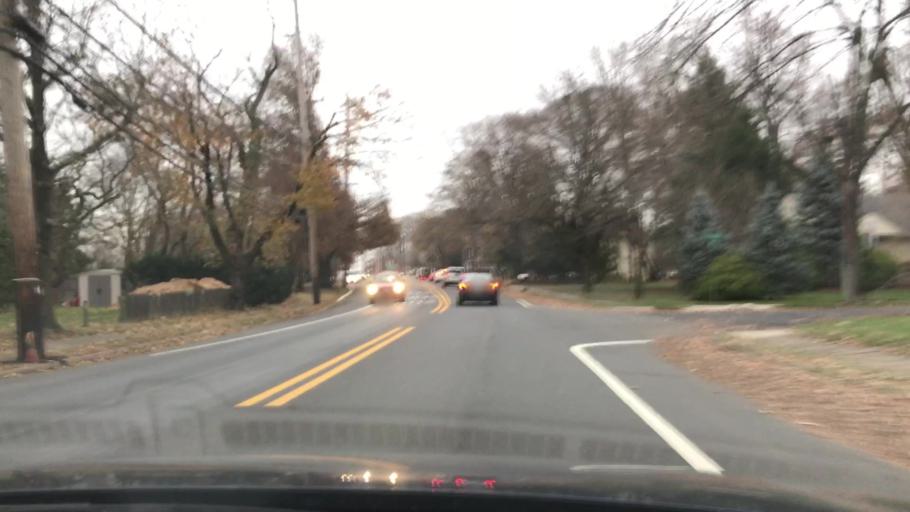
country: US
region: New Jersey
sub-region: Bergen County
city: Paramus
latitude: 40.9698
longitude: -74.0837
